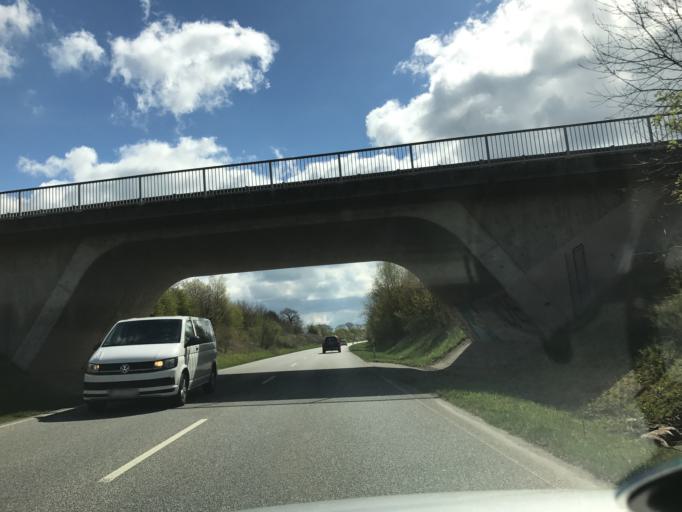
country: DE
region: Schleswig-Holstein
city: Schellhorn
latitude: 54.2452
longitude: 10.3028
